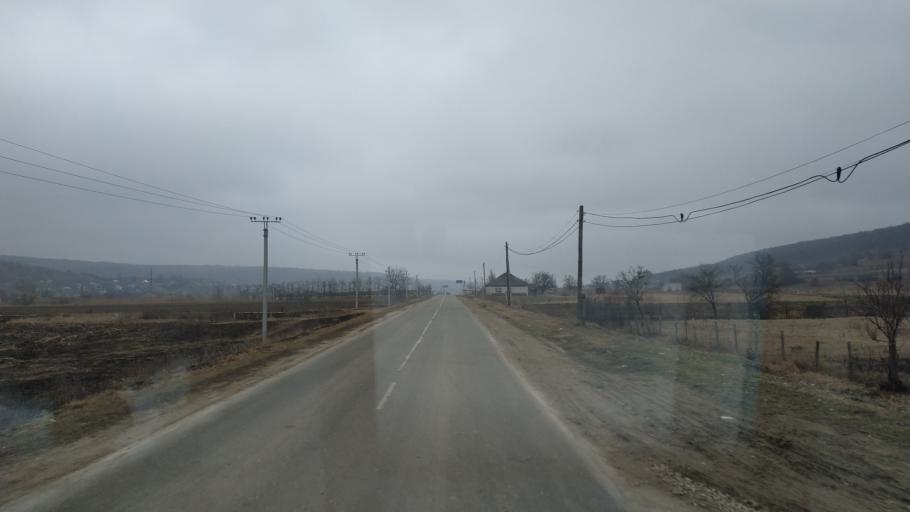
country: MD
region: Hincesti
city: Hincesti
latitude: 46.9579
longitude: 28.4887
